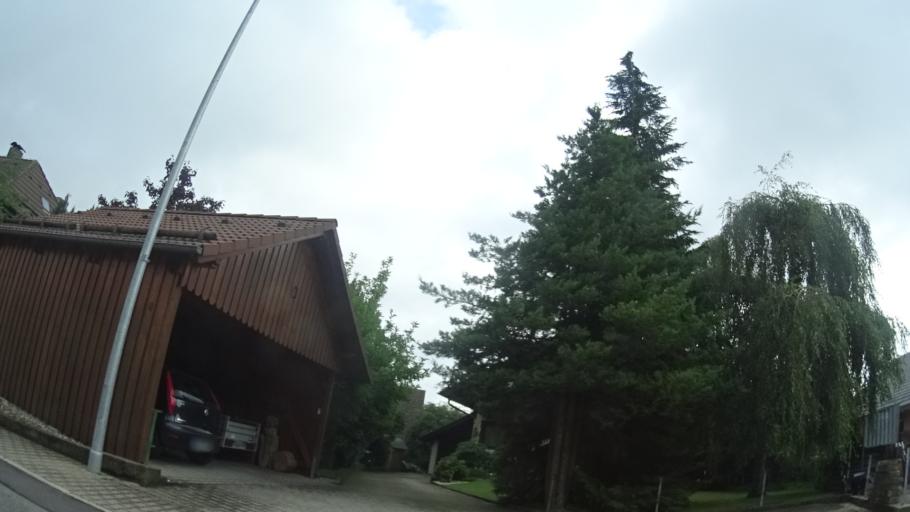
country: DE
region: Baden-Wuerttemberg
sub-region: Karlsruhe Region
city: Dobel
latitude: 48.8169
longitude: 8.4799
